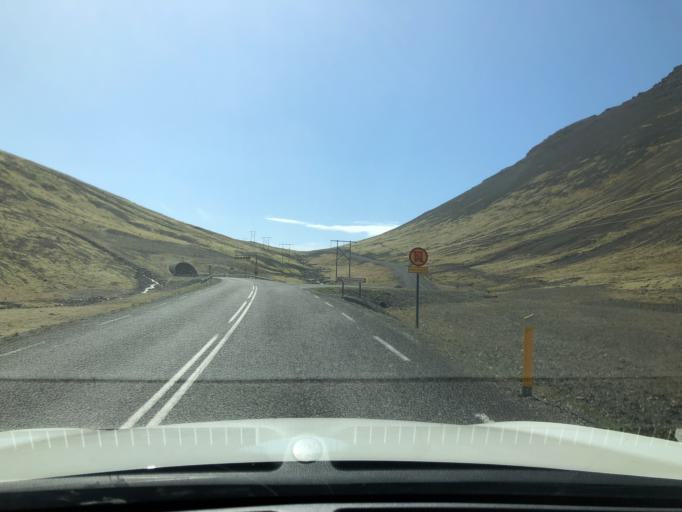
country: IS
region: East
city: Hoefn
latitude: 64.2943
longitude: -15.0267
